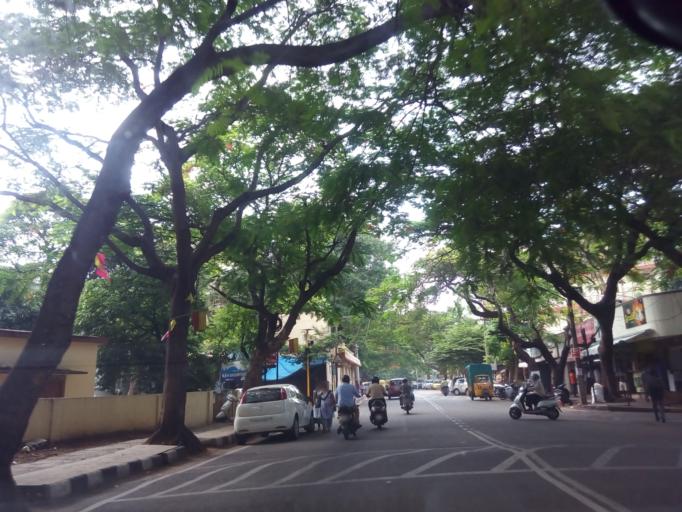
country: IN
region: Karnataka
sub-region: Bangalore Urban
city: Bangalore
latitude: 13.0073
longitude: 77.5641
